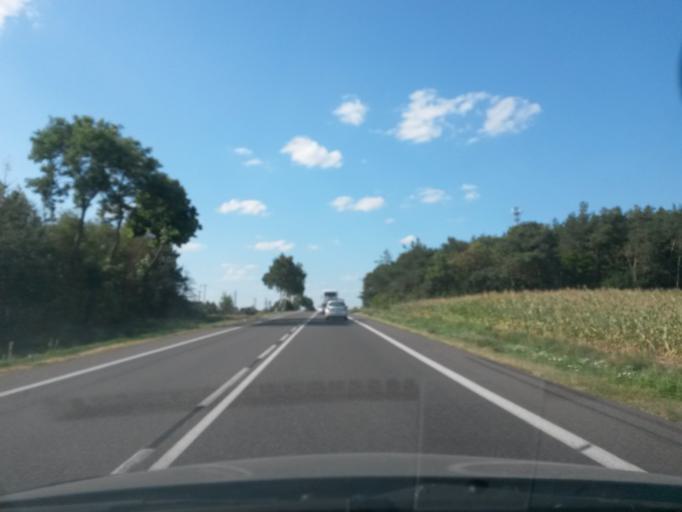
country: PL
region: Masovian Voivodeship
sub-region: Powiat plocki
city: Starozreby
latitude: 52.6517
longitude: 20.0869
